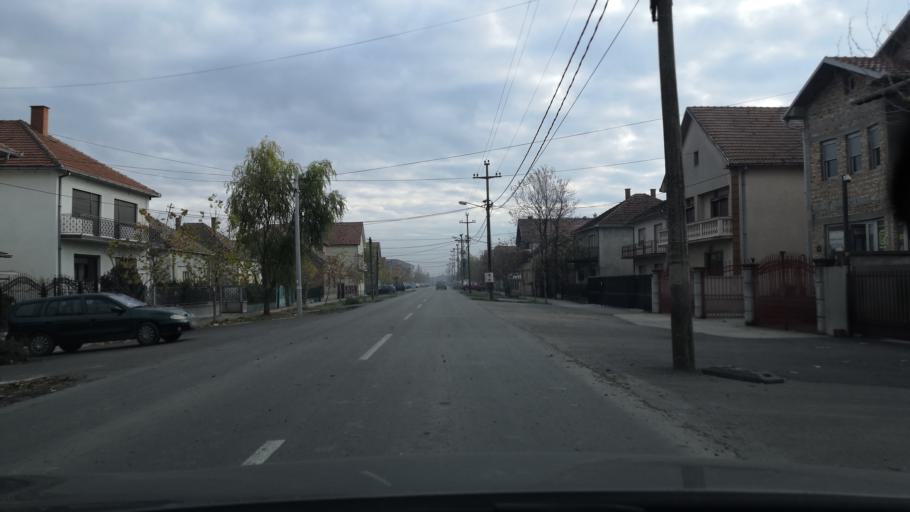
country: RS
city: Ugrinovci
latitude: 44.8741
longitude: 20.1914
